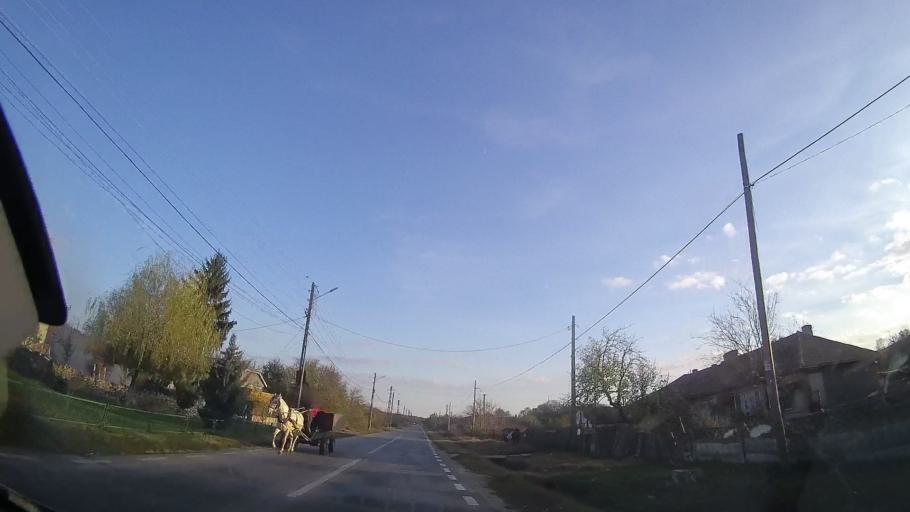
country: RO
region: Constanta
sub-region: Comuna Chirnogeni
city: Plopeni
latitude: 43.9511
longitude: 28.1972
